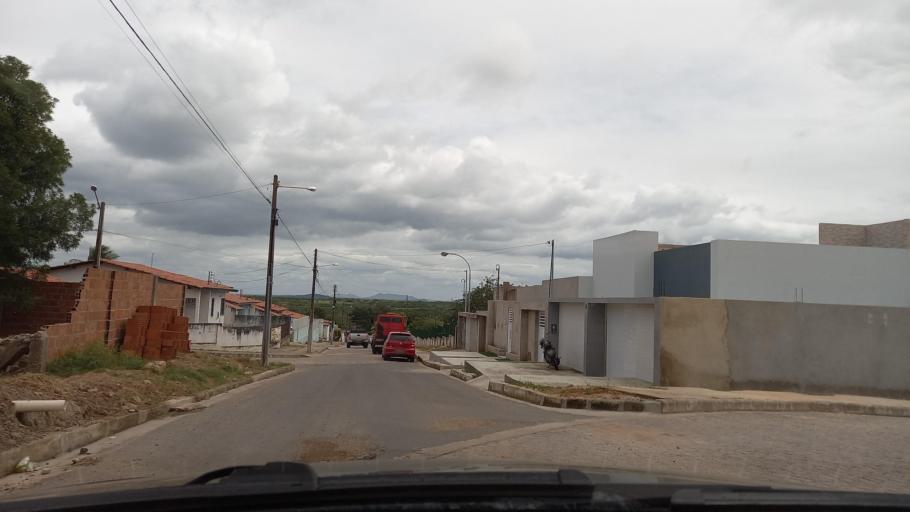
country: BR
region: Sergipe
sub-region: Caninde De Sao Francisco
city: Caninde de Sao Francisco
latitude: -9.6134
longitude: -37.7652
